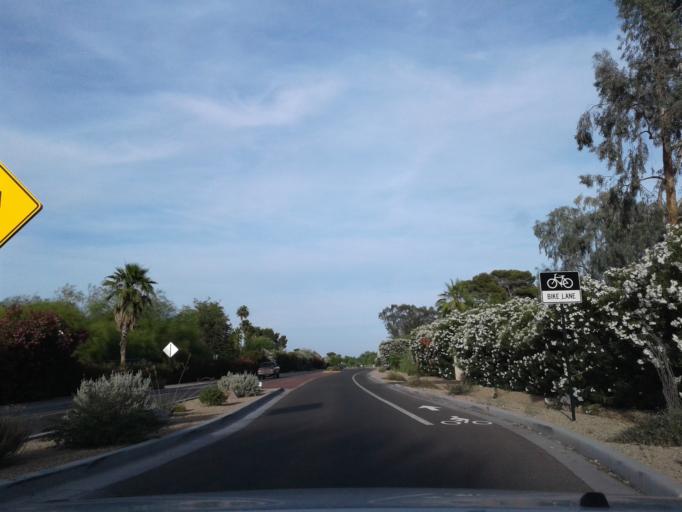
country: US
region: Arizona
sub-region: Maricopa County
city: Paradise Valley
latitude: 33.5608
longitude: -111.9691
